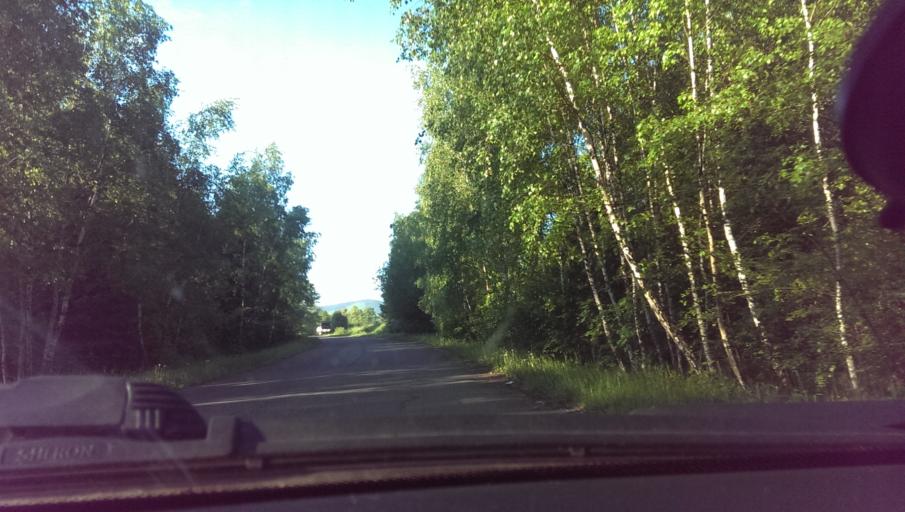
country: CZ
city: Ticha
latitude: 49.5513
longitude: 18.2345
